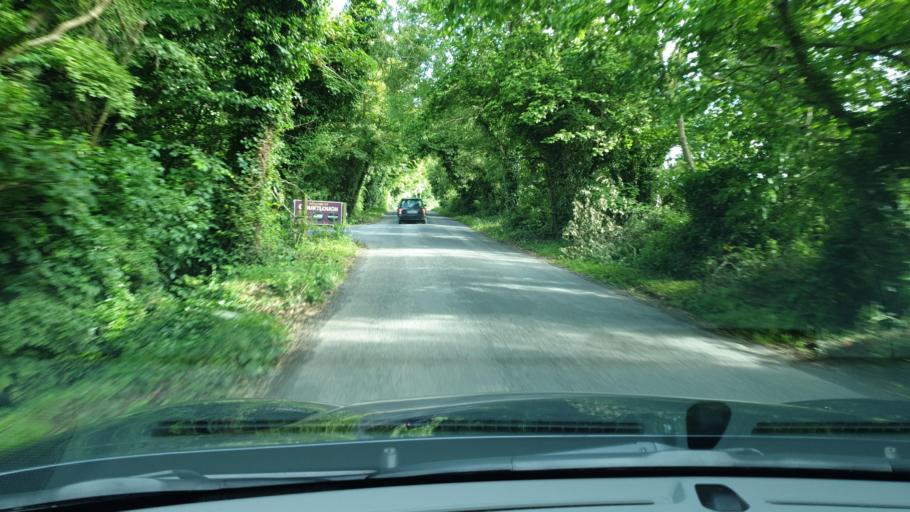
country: IE
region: Leinster
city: Balrothery
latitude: 53.5705
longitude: -6.2002
